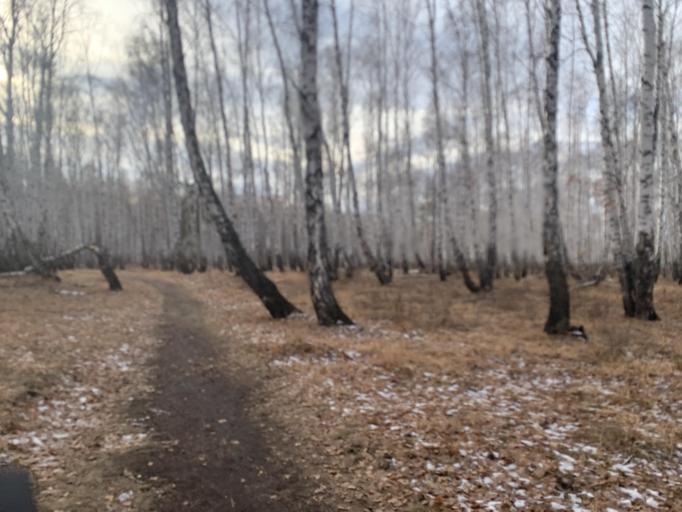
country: RU
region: Chelyabinsk
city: Roshchino
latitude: 55.2030
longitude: 61.3040
